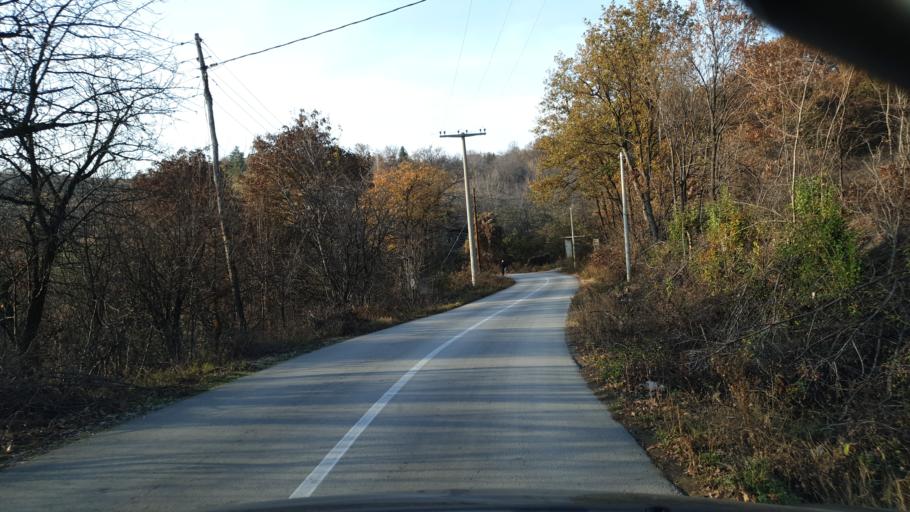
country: RS
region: Central Serbia
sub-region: Borski Okrug
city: Bor
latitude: 44.0485
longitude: 22.0868
